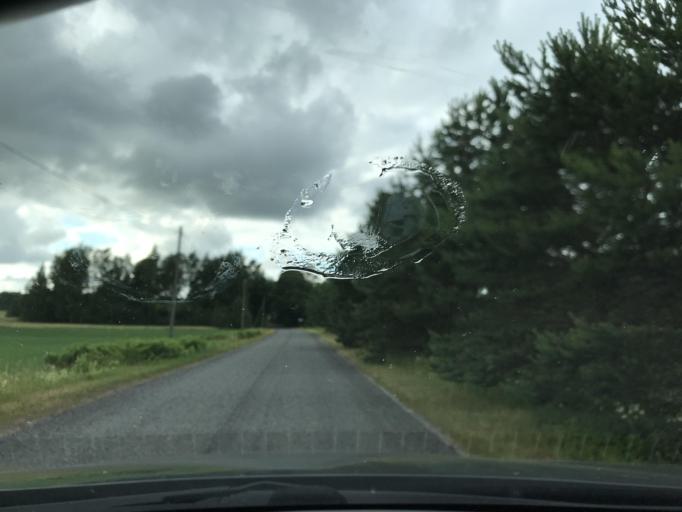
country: LV
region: Alsunga
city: Alsunga
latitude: 56.9760
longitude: 21.6398
